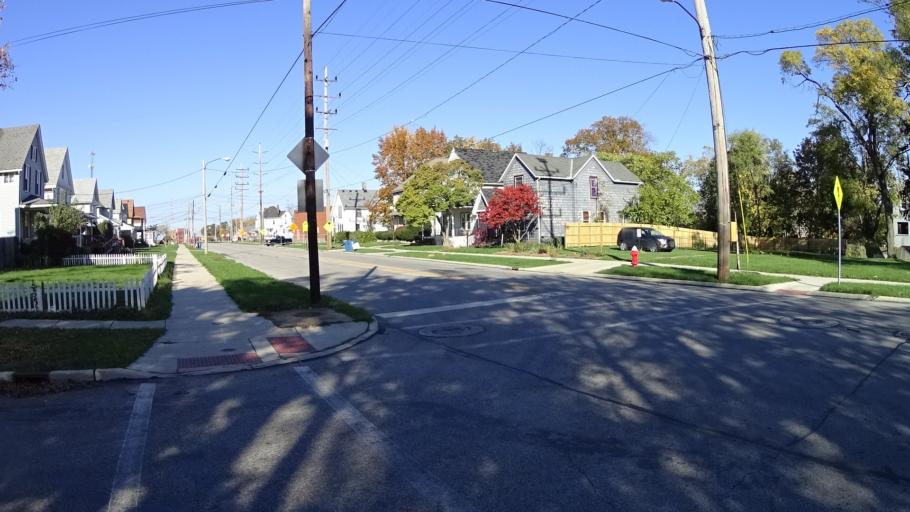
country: US
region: Ohio
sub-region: Lorain County
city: Lorain
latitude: 41.4649
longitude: -82.1850
